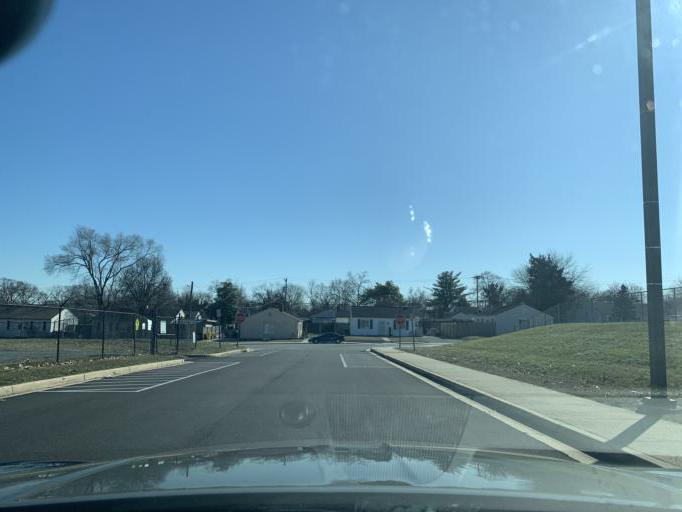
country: US
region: Maryland
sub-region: Anne Arundel County
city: Glen Burnie
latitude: 39.1577
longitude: -76.6162
